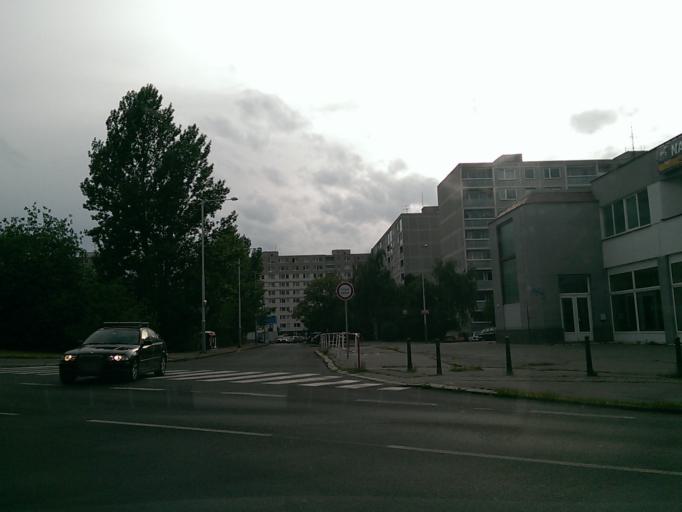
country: CZ
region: Central Bohemia
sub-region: Okres Praha-Zapad
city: Pruhonice
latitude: 50.0384
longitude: 14.5097
